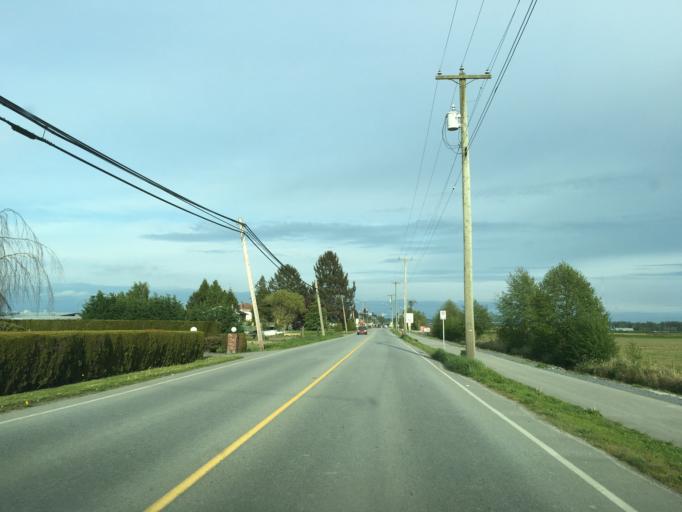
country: CA
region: British Columbia
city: Ladner
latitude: 49.1699
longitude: -123.0279
